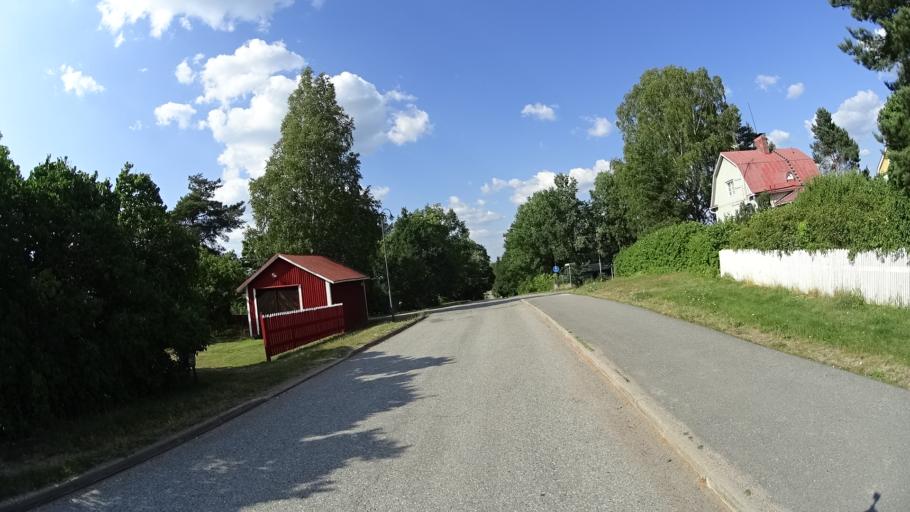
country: FI
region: Uusimaa
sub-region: Porvoo
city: Porvoo
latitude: 60.4015
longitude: 25.6651
